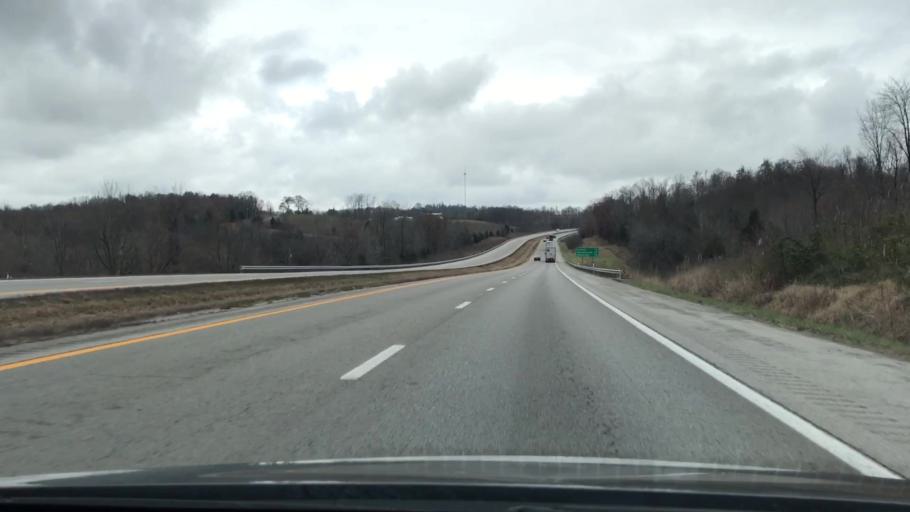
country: US
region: Kentucky
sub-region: Christian County
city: Hopkinsville
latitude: 36.9108
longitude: -87.4741
